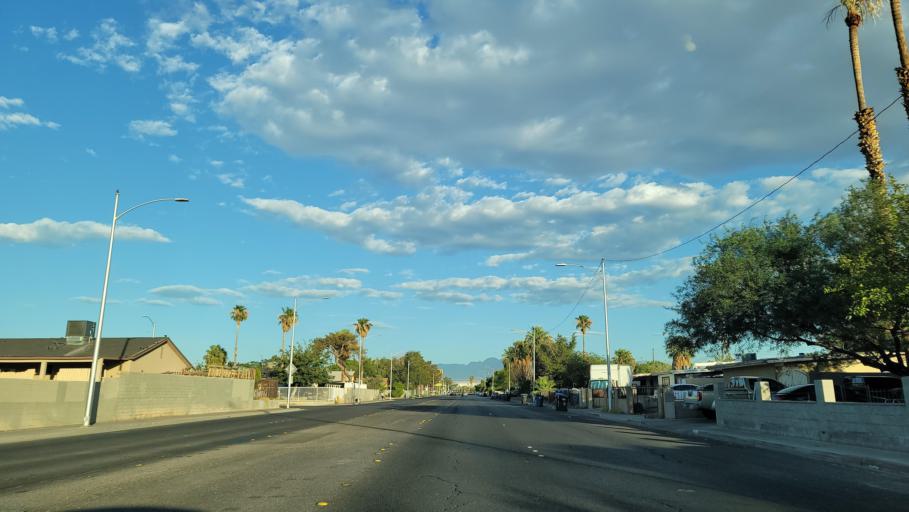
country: US
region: Nevada
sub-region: Clark County
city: North Las Vegas
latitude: 36.1884
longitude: -115.1095
